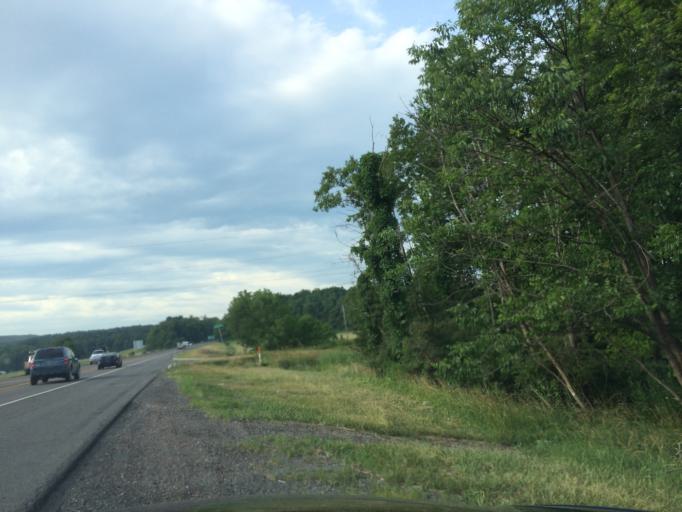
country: US
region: Maryland
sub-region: Allegany County
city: Frostburg
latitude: 39.6276
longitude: -78.9163
